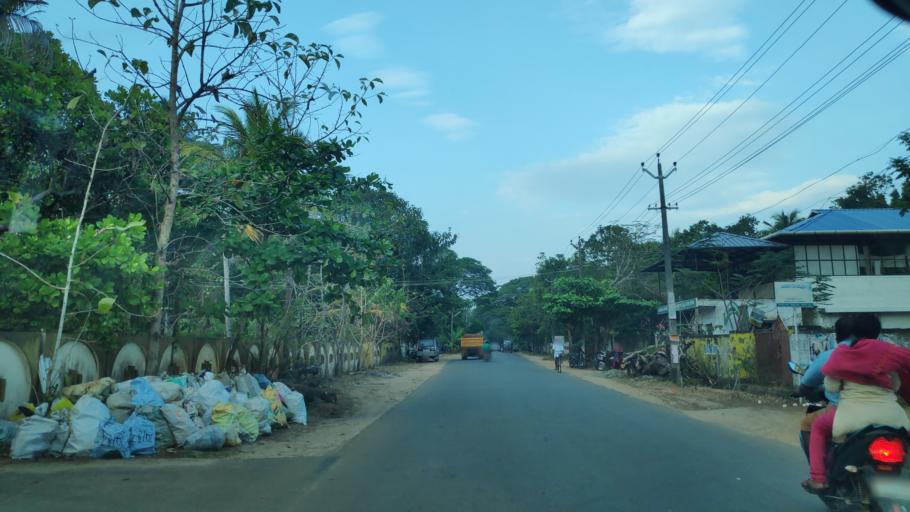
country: IN
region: Kerala
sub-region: Alappuzha
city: Shertallai
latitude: 9.6531
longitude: 76.3745
